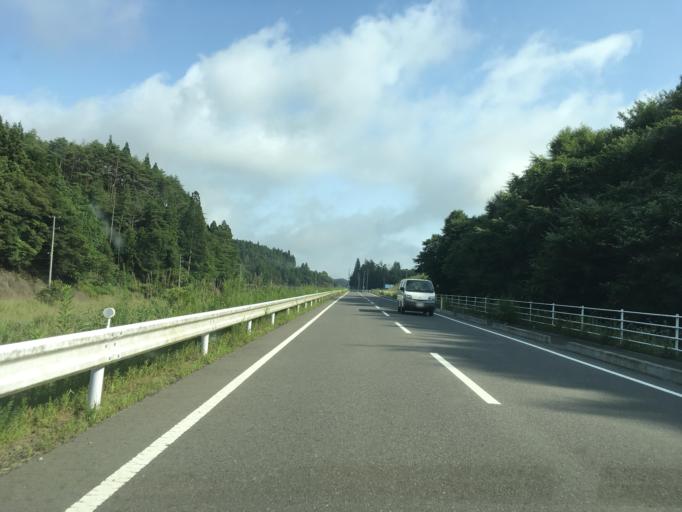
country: JP
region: Iwate
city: Ofunato
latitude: 38.9061
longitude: 141.6222
